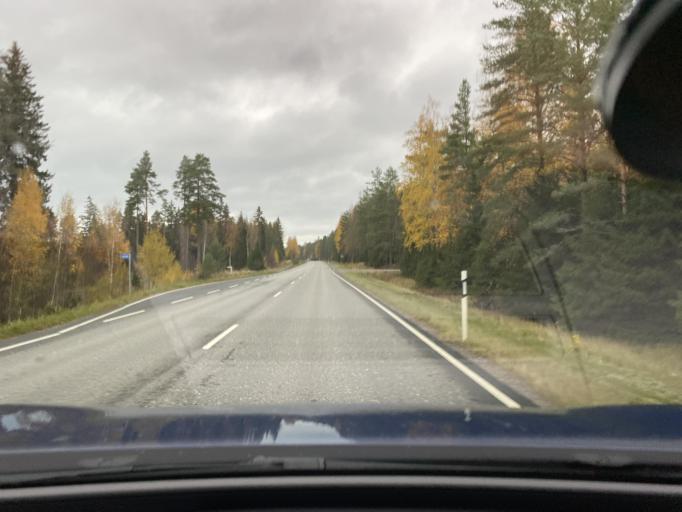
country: FI
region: Varsinais-Suomi
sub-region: Loimaa
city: Ylaene
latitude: 60.9140
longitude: 22.4150
